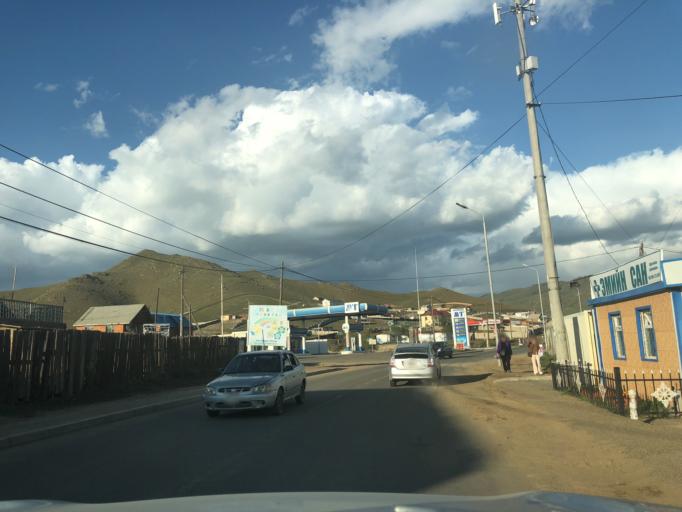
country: MN
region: Ulaanbaatar
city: Ulaanbaatar
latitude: 47.9277
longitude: 107.1440
